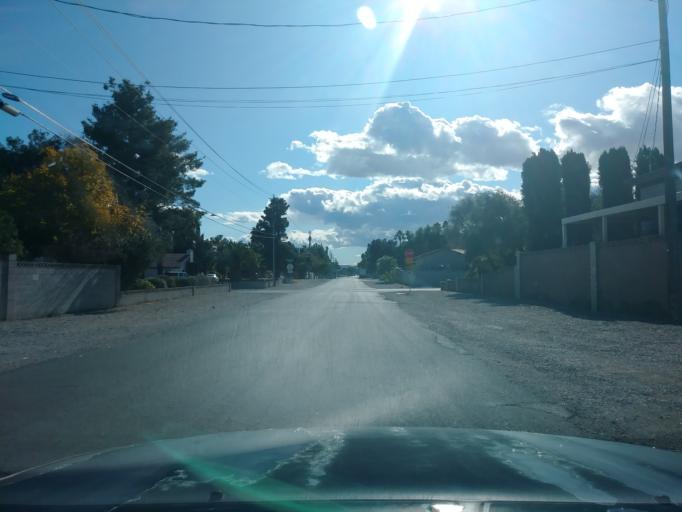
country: US
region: Nevada
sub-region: Clark County
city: Spring Valley
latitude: 36.1486
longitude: -115.2146
